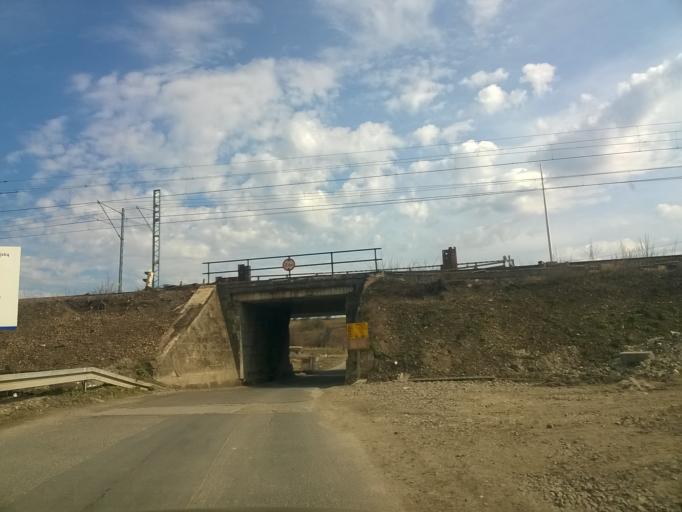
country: PL
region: Lesser Poland Voivodeship
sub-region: Powiat krakowski
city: Rzaska
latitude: 50.0861
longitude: 19.8524
